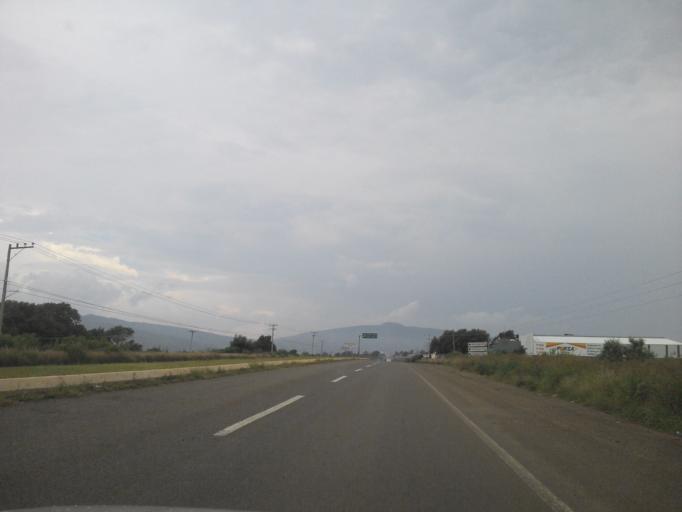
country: MX
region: Jalisco
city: San Jose de Gracia
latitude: 20.7347
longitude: -102.5001
